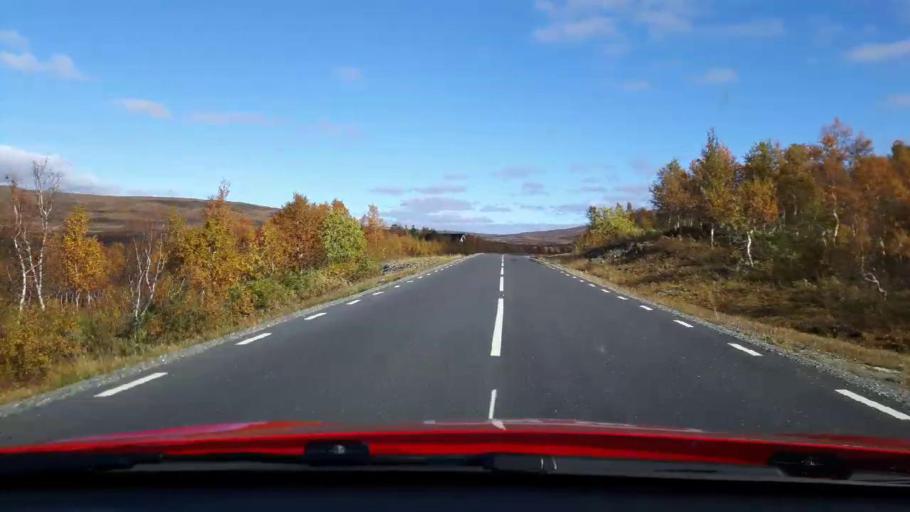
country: NO
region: Nordland
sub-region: Hattfjelldal
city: Hattfjelldal
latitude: 65.0087
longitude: 14.2698
